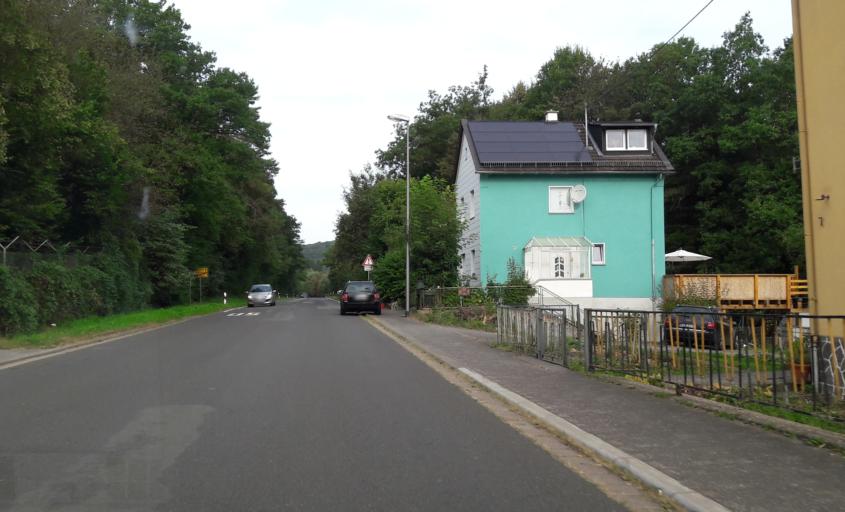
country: DE
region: Rheinland-Pfalz
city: Ellweiler
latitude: 49.6092
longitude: 7.1736
